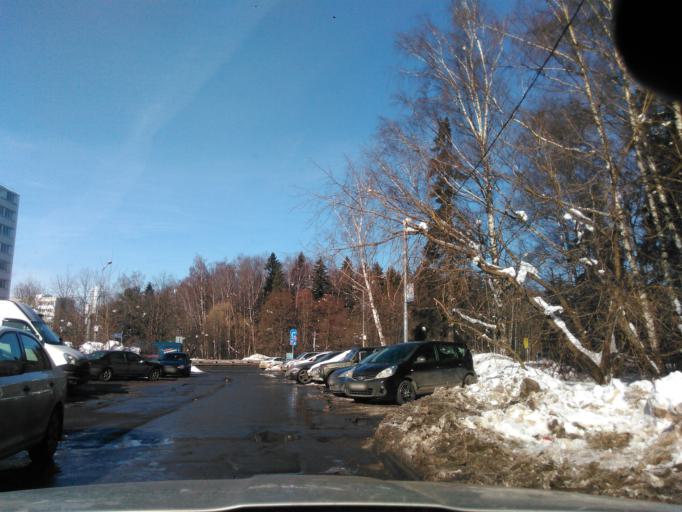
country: RU
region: Moscow
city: Zelenograd
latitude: 55.9798
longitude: 37.1941
